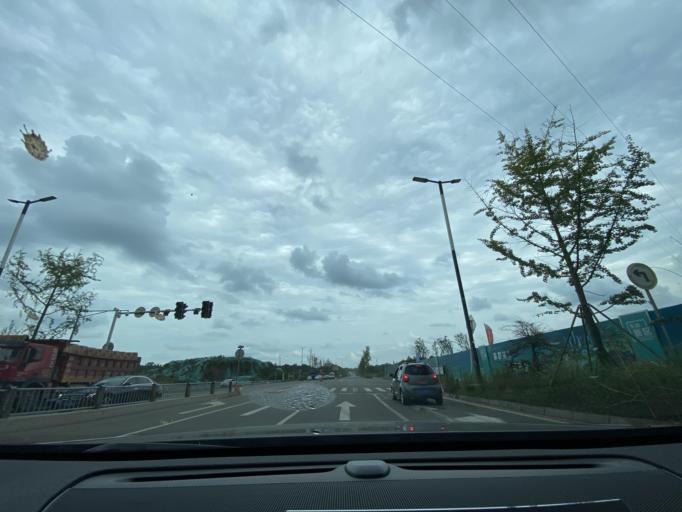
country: CN
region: Sichuan
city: Jiancheng
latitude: 30.4928
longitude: 104.4670
